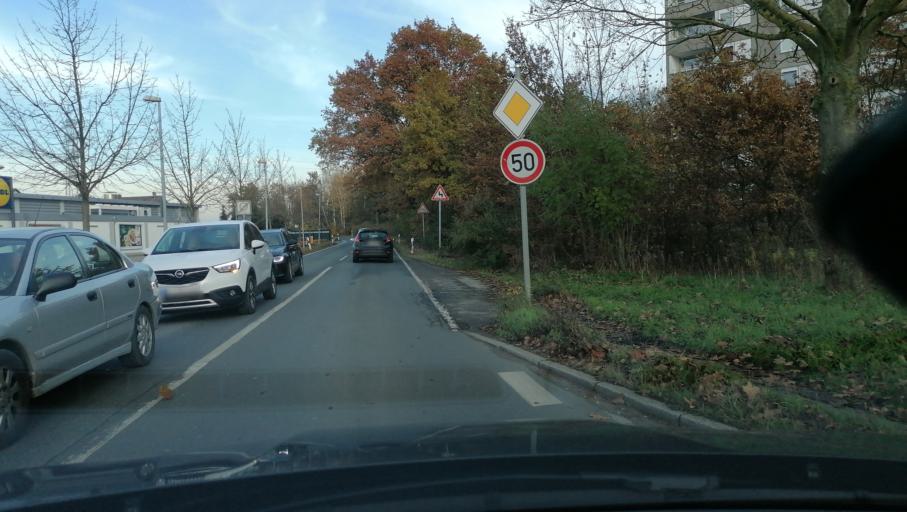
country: DE
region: North Rhine-Westphalia
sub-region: Regierungsbezirk Arnsberg
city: Herne
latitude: 51.5702
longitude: 7.2416
